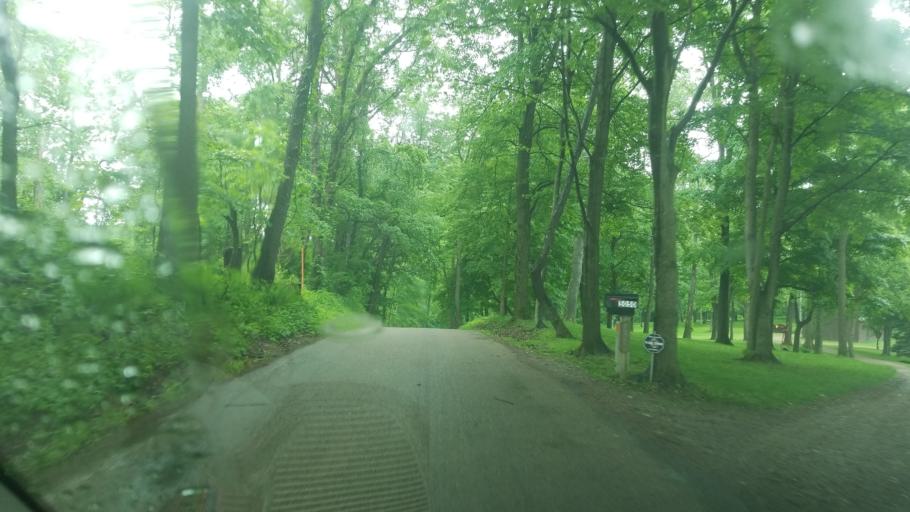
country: US
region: Ohio
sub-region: Sandusky County
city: Bellville
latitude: 40.6199
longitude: -82.4650
